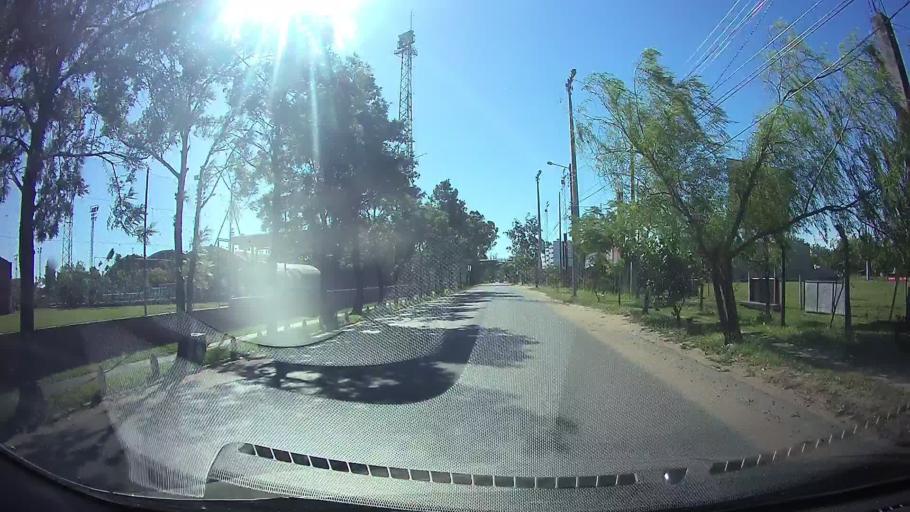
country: PY
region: Central
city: Fernando de la Mora
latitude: -25.2864
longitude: -57.5432
